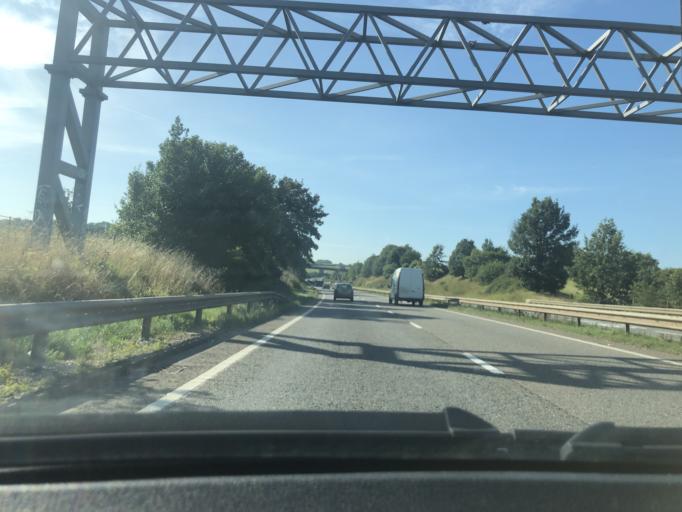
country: GB
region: England
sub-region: Devon
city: Exminster
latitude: 50.6854
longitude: -3.5239
